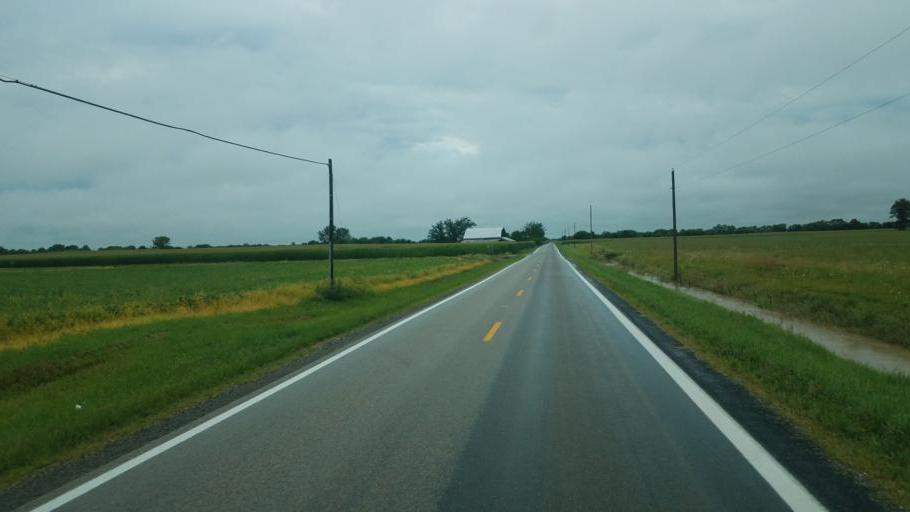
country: US
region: Ohio
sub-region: Union County
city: Richwood
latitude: 40.5263
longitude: -83.3495
